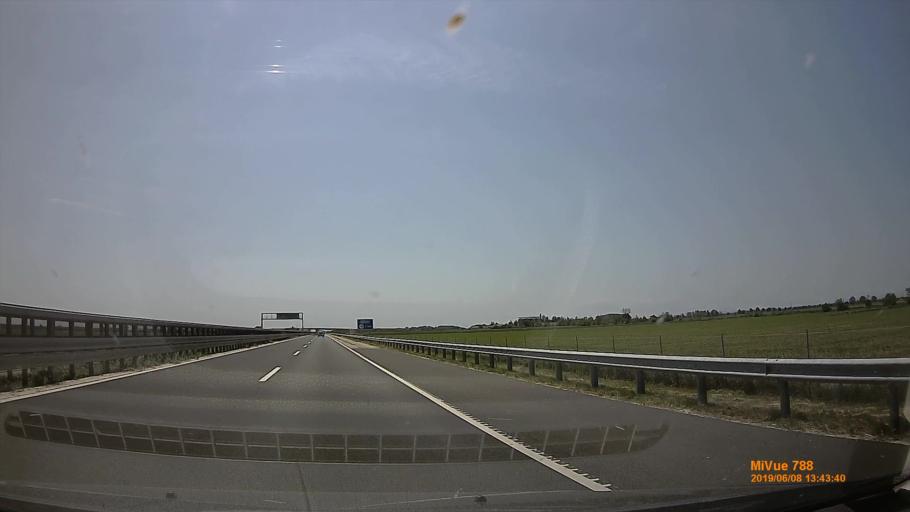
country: HU
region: Gyor-Moson-Sopron
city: Beled
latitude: 47.4489
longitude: 17.1000
